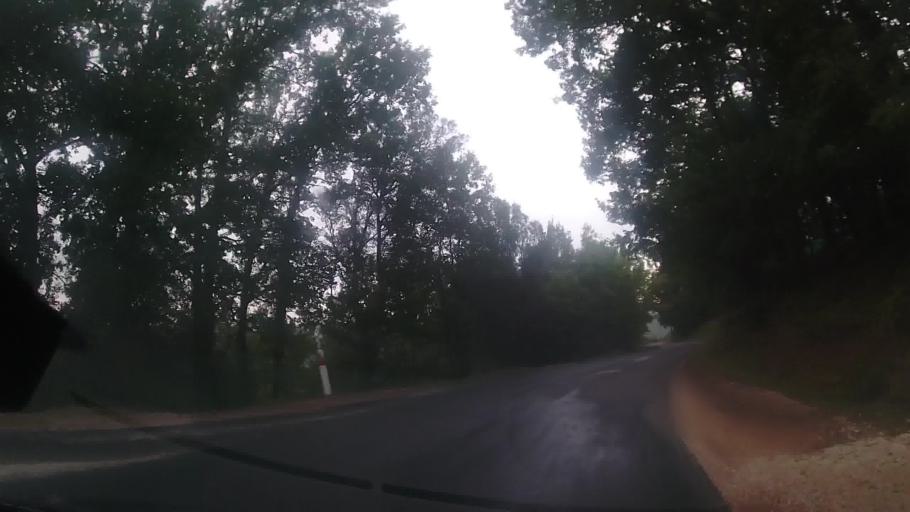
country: FR
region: Aquitaine
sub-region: Departement de la Dordogne
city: Cenac-et-Saint-Julien
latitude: 44.7868
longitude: 1.1864
